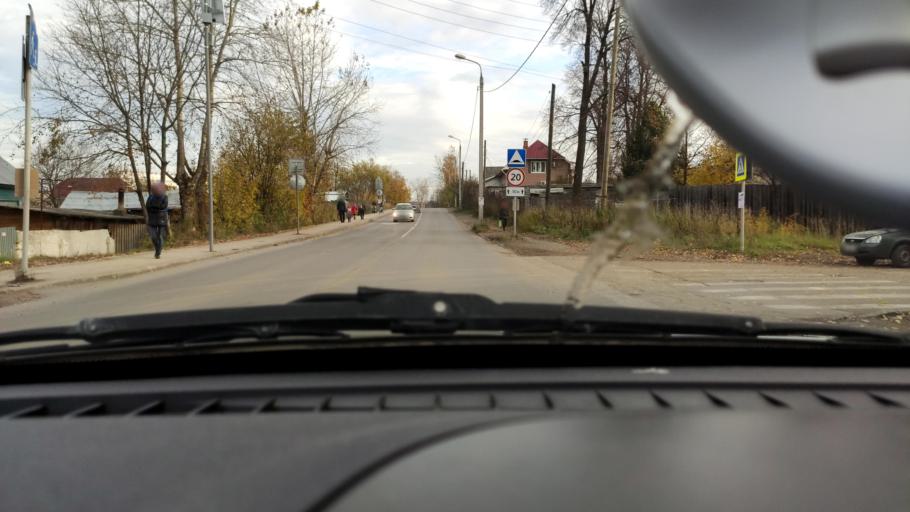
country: RU
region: Perm
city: Perm
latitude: 58.0868
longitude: 56.3984
